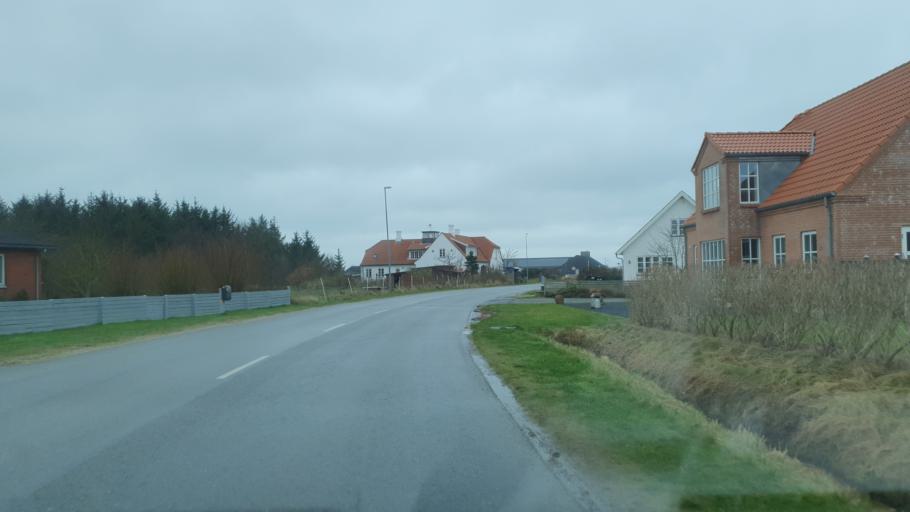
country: DK
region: North Denmark
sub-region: Jammerbugt Kommune
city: Fjerritslev
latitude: 57.1373
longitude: 9.1261
